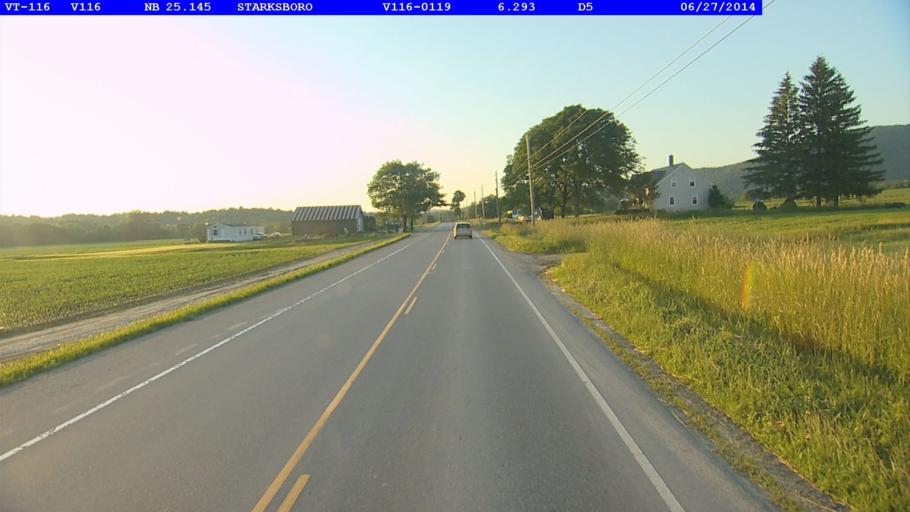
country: US
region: Vermont
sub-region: Chittenden County
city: Hinesburg
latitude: 44.2746
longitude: -73.0673
